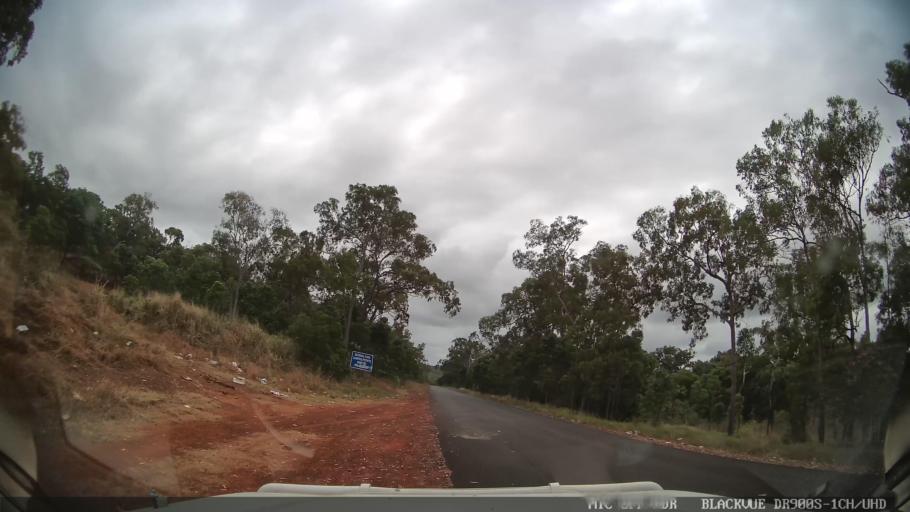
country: AU
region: Queensland
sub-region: Cook
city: Cooktown
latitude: -15.3314
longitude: 145.0339
